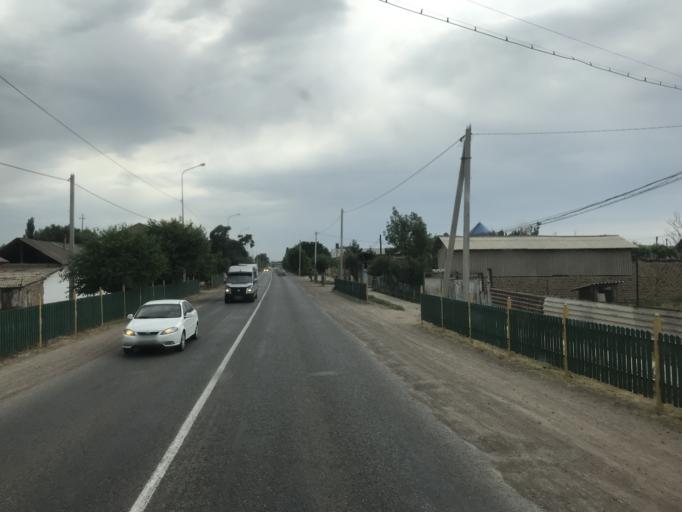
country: KZ
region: Ongtustik Qazaqstan
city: Saryaghash
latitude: 41.3513
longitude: 68.9659
